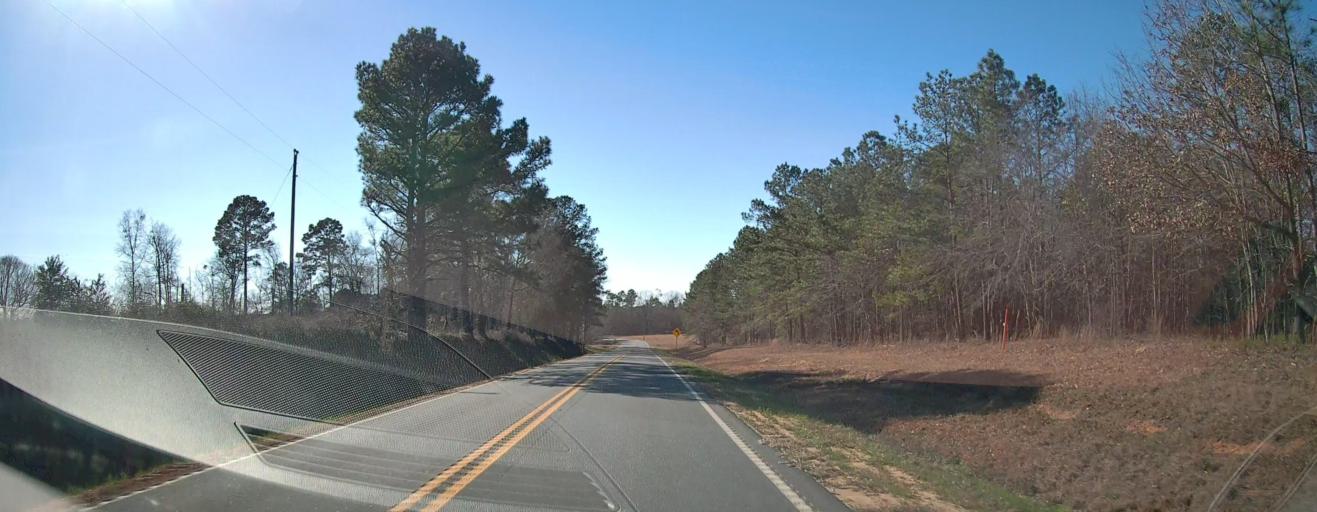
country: US
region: Georgia
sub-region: Taylor County
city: Butler
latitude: 32.6608
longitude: -84.3405
